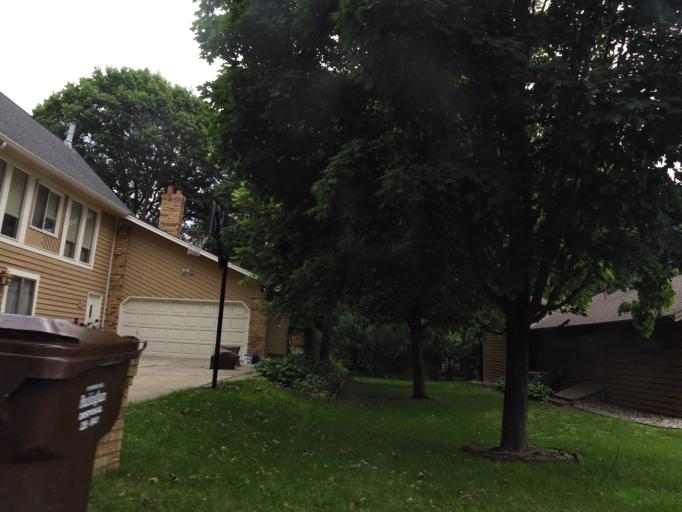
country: US
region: Minnesota
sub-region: Scott County
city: Prior Lake
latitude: 44.7087
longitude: -93.4449
